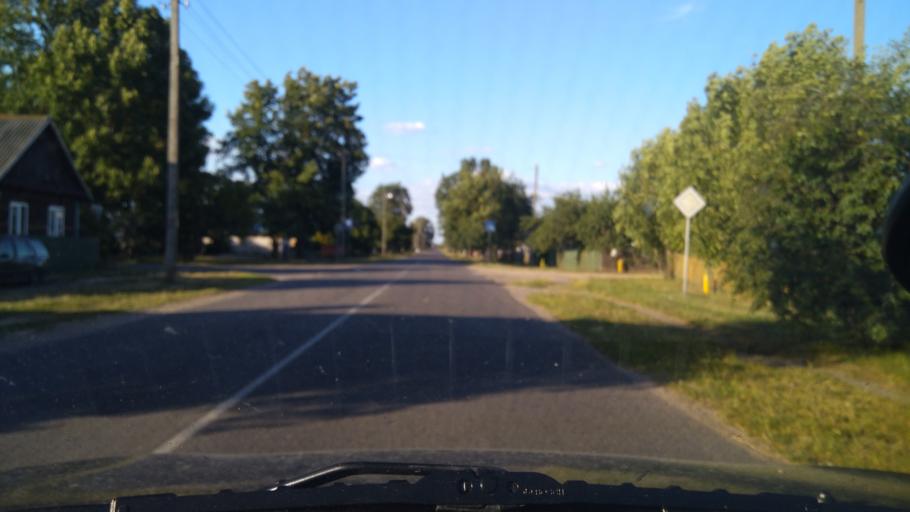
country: BY
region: Brest
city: Byaroza
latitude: 52.5847
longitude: 24.8647
